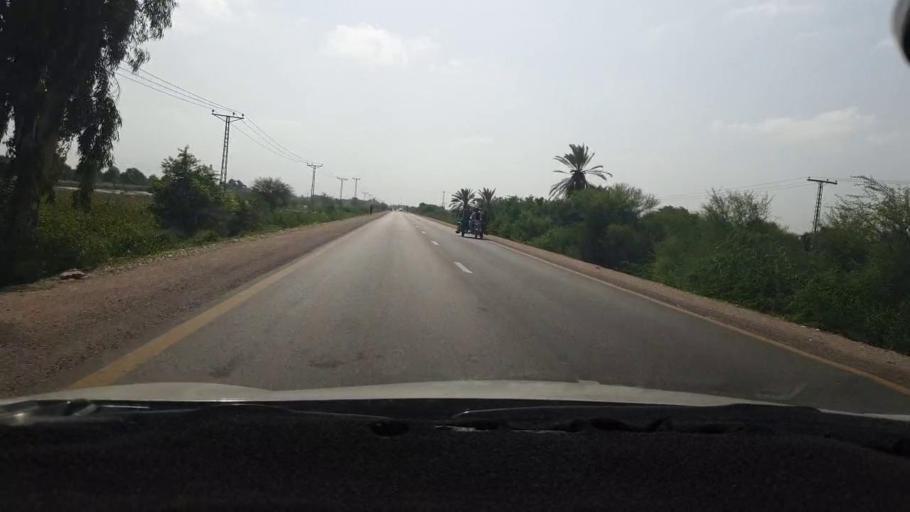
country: PK
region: Sindh
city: Mirpur Khas
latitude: 25.7351
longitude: 69.1011
